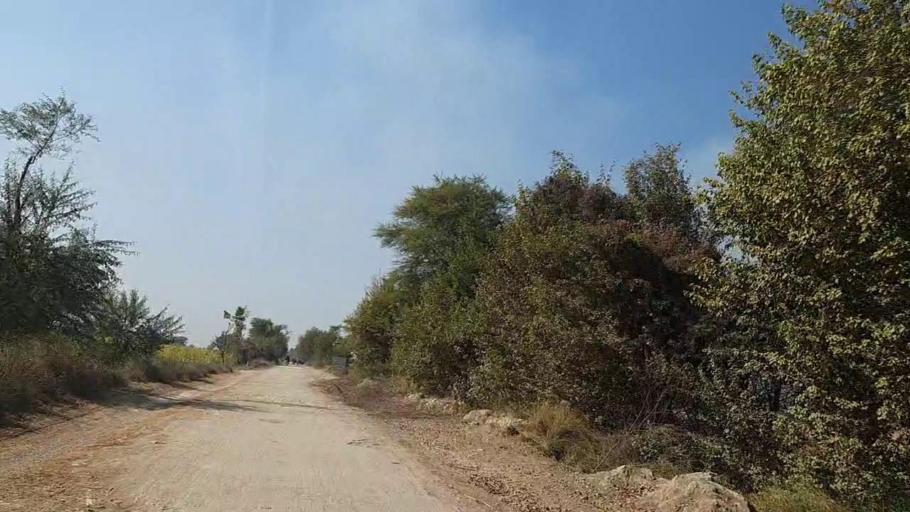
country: PK
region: Sindh
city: Daulatpur
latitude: 26.2905
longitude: 68.0715
